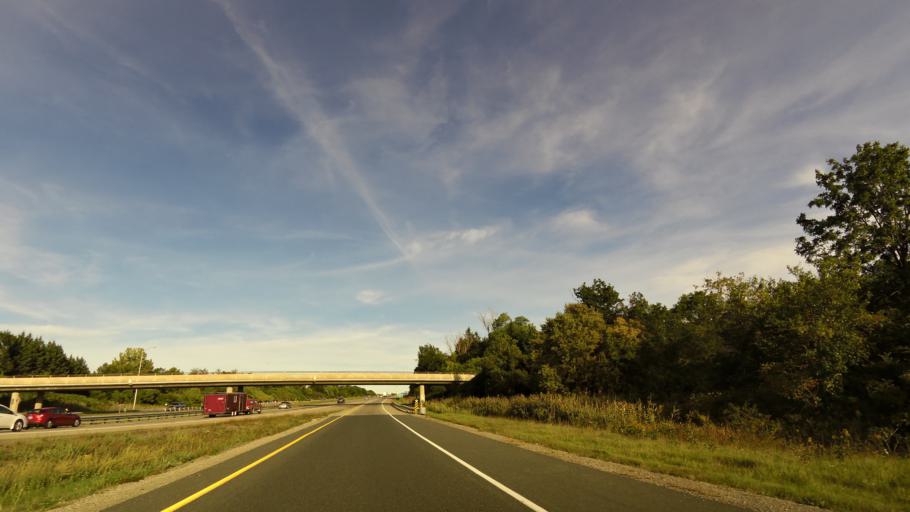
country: CA
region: Ontario
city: Ancaster
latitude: 43.2044
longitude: -80.0026
